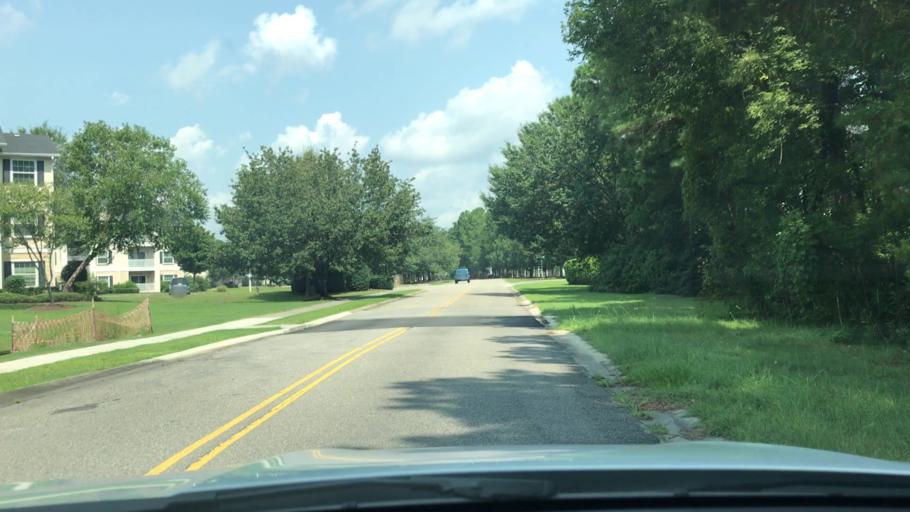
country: US
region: South Carolina
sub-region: Horry County
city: Forestbrook
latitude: 33.7792
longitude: -78.9651
